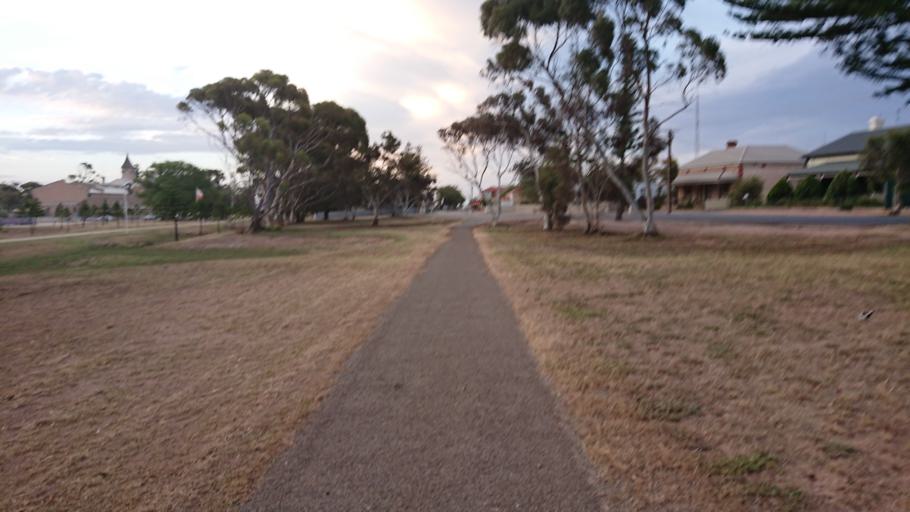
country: AU
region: South Australia
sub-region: Copper Coast
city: Wallaroo
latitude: -33.9339
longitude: 137.6300
